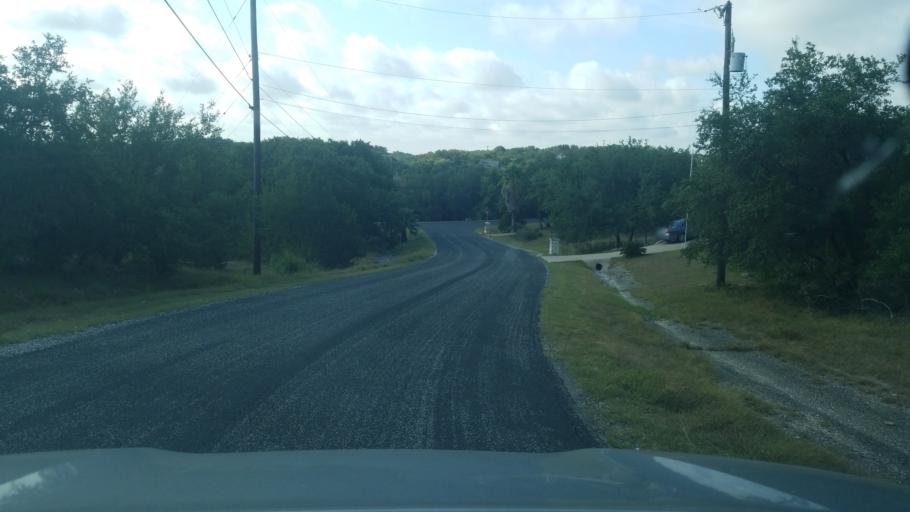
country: US
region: Texas
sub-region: Bexar County
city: Timberwood Park
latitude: 29.6856
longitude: -98.5048
